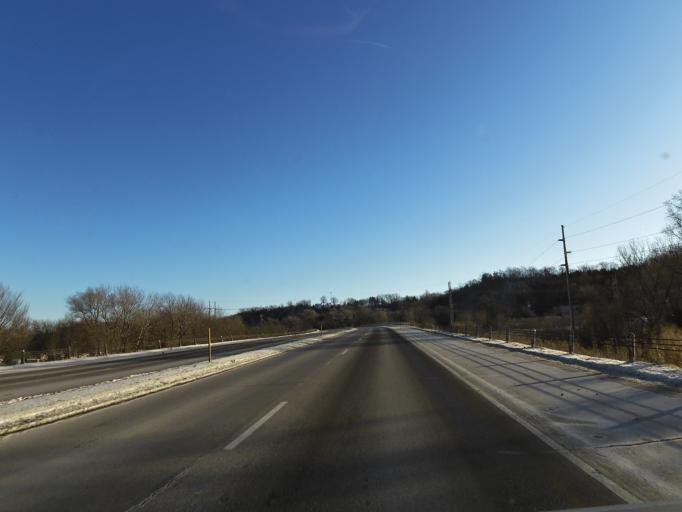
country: US
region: Minnesota
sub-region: Scott County
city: Jordan
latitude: 44.6731
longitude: -93.6301
